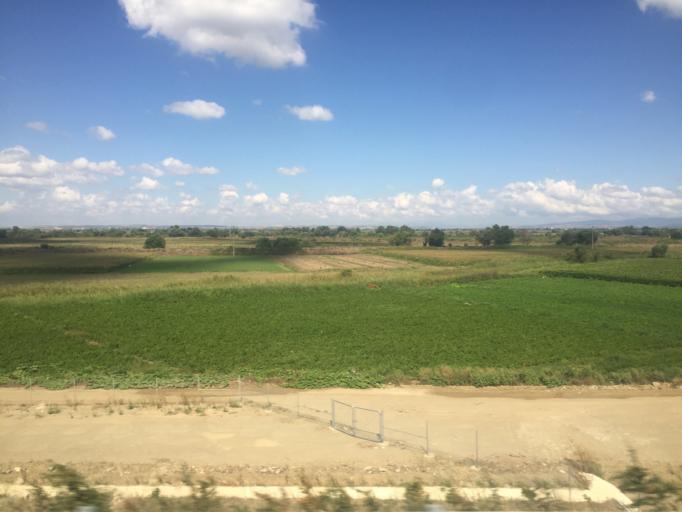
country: TR
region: Bursa
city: Karacabey
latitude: 40.1286
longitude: 28.2882
